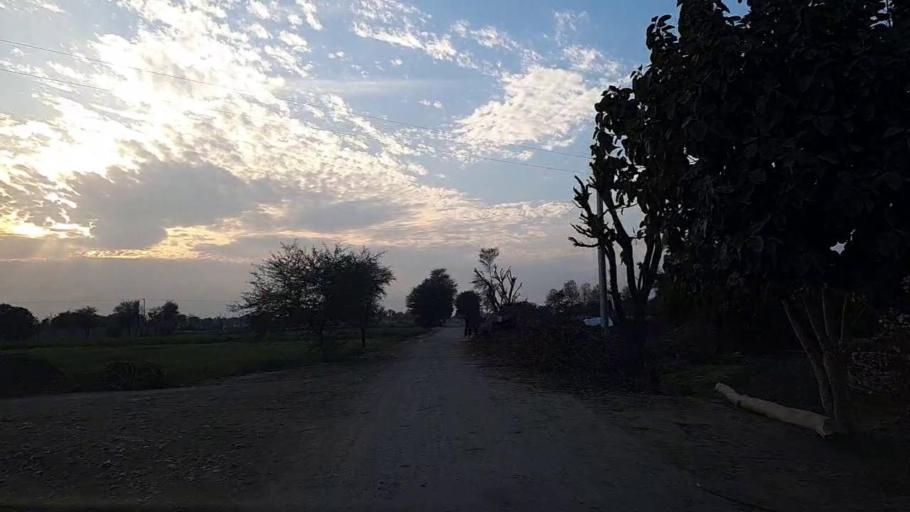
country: PK
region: Sindh
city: Daur
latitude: 26.4168
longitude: 68.4907
